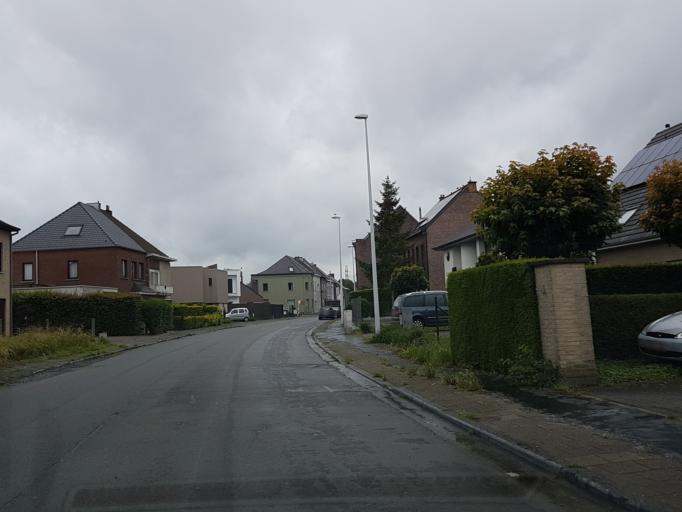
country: BE
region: Flanders
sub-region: Provincie Oost-Vlaanderen
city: Aalst
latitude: 50.9577
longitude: 4.0508
